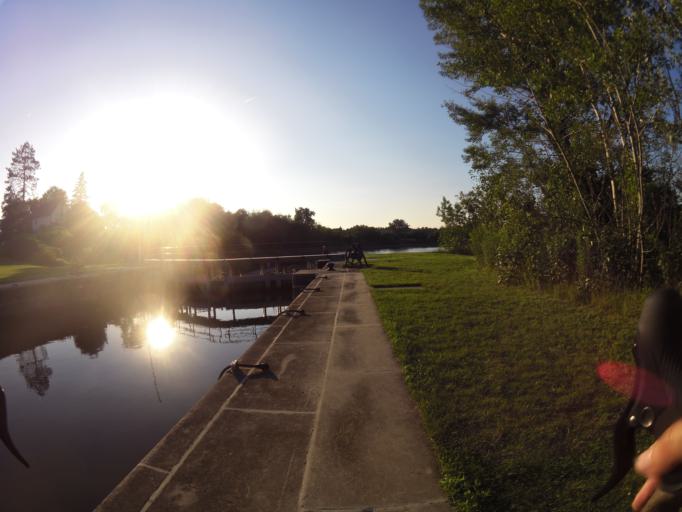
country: CA
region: Ontario
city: Ottawa
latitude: 45.3215
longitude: -75.6980
